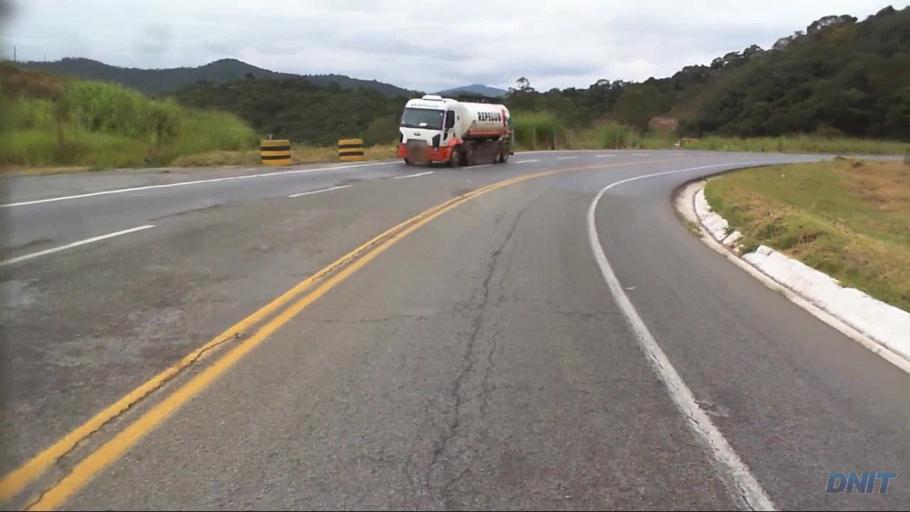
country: BR
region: Minas Gerais
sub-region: Joao Monlevade
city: Joao Monlevade
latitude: -19.8552
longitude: -43.2238
